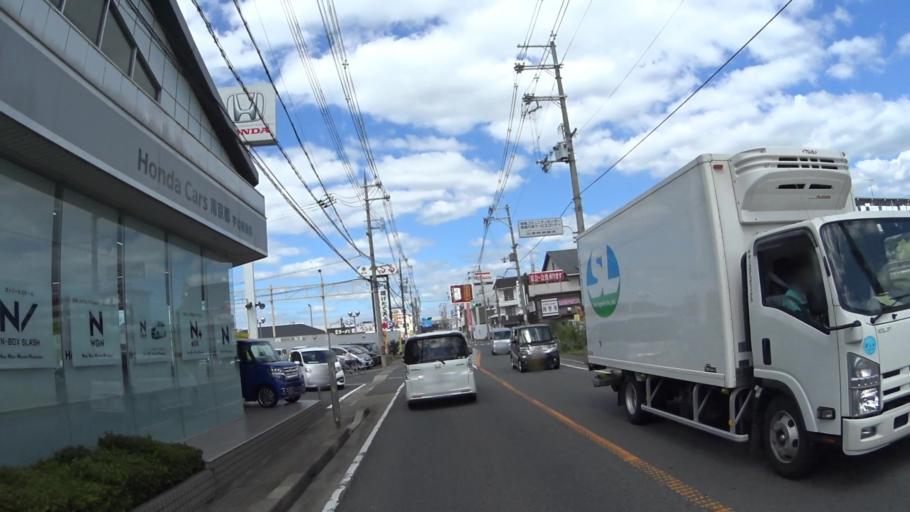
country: JP
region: Kyoto
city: Uji
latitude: 34.9052
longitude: 135.7837
